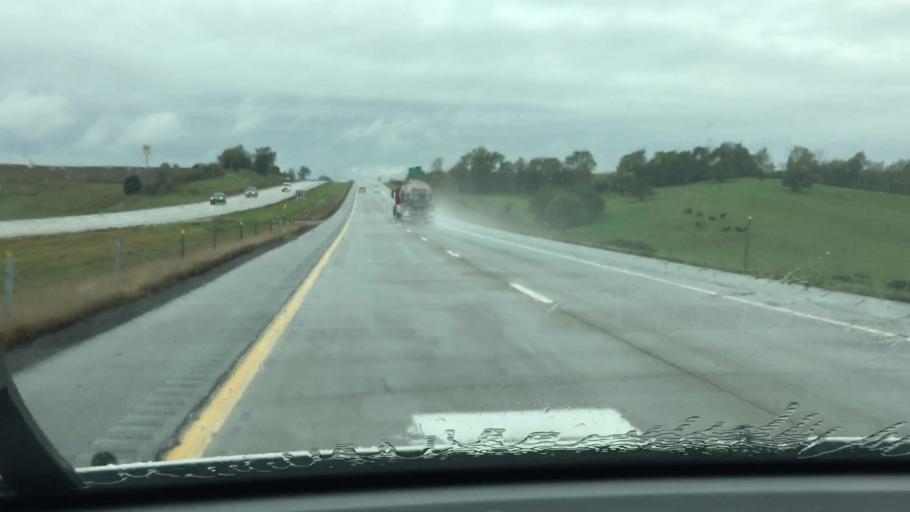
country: US
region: Iowa
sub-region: Poweshiek County
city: Brooklyn
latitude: 41.6957
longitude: -92.3447
